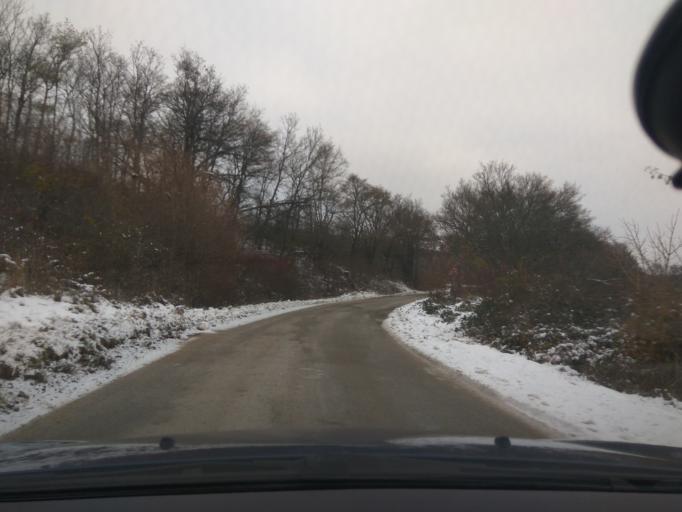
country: SK
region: Nitriansky
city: Stara Tura
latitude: 48.8177
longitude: 17.7070
